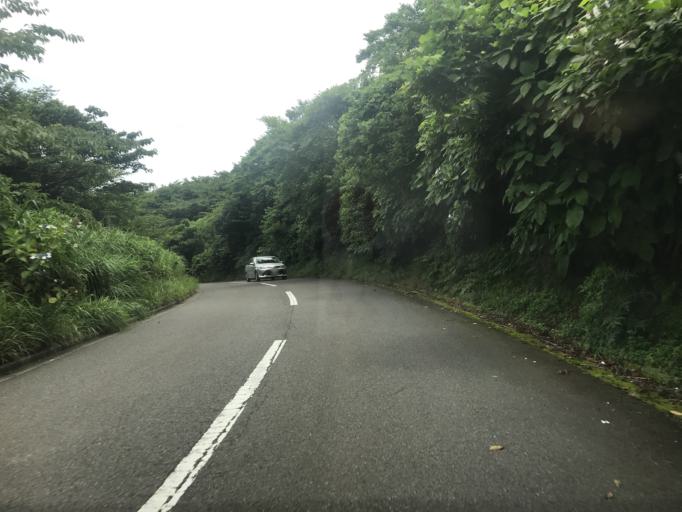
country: JP
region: Shizuoka
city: Ito
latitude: 34.7592
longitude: 139.4084
